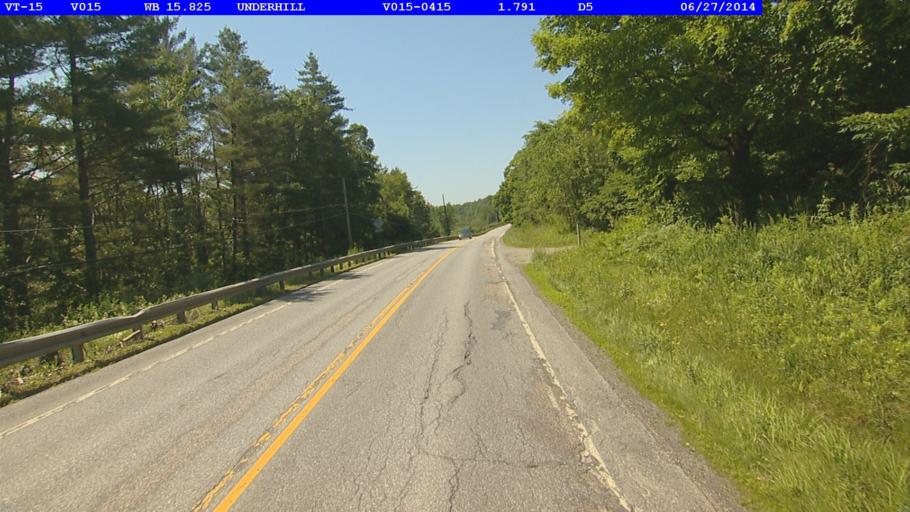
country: US
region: Vermont
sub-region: Chittenden County
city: Jericho
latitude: 44.5497
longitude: -72.9455
